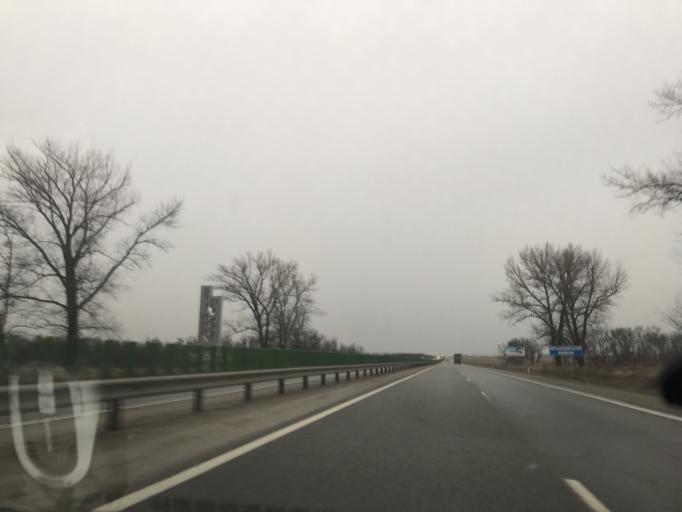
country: RU
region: Krasnodarskiy
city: Pavlovskaya
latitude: 46.2309
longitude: 39.8315
